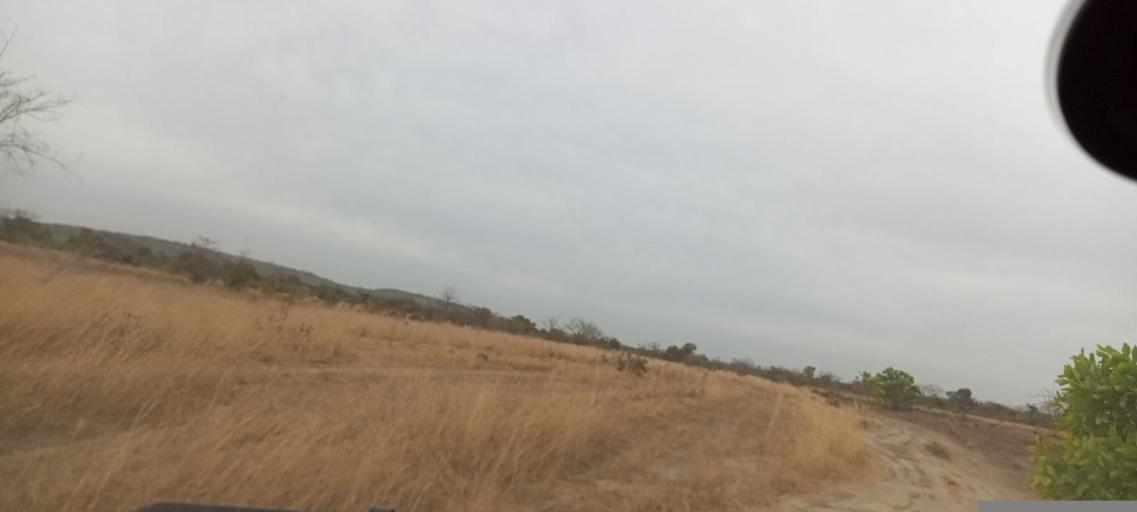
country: ML
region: Koulikoro
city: Kati
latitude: 12.7708
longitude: -8.3811
